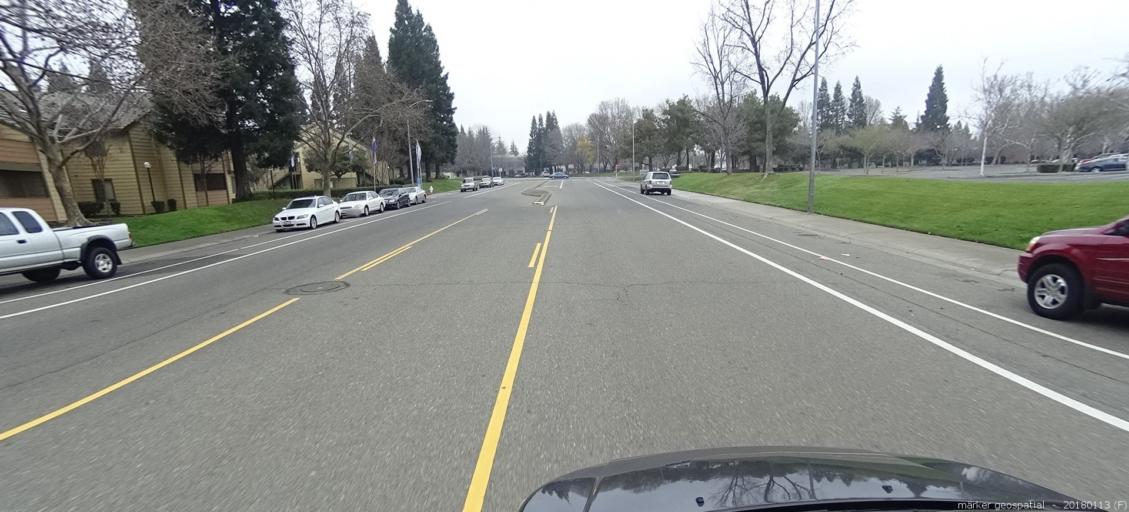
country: US
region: California
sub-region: Sacramento County
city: Rancho Cordova
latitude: 38.5831
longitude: -121.2924
